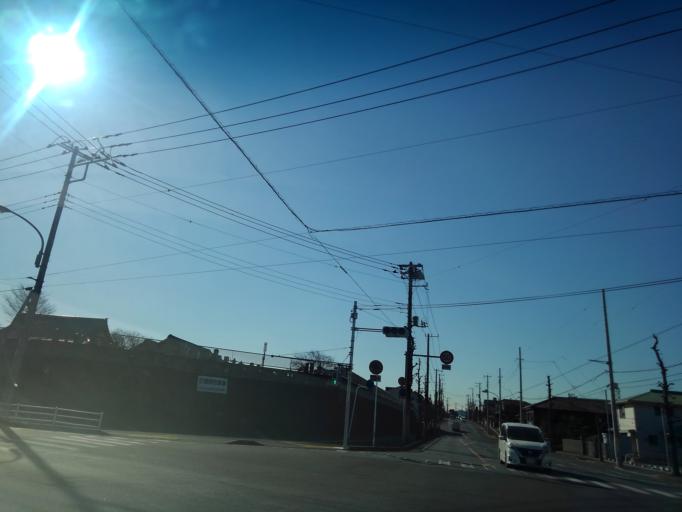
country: JP
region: Chiba
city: Kimitsu
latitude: 35.3320
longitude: 139.9163
